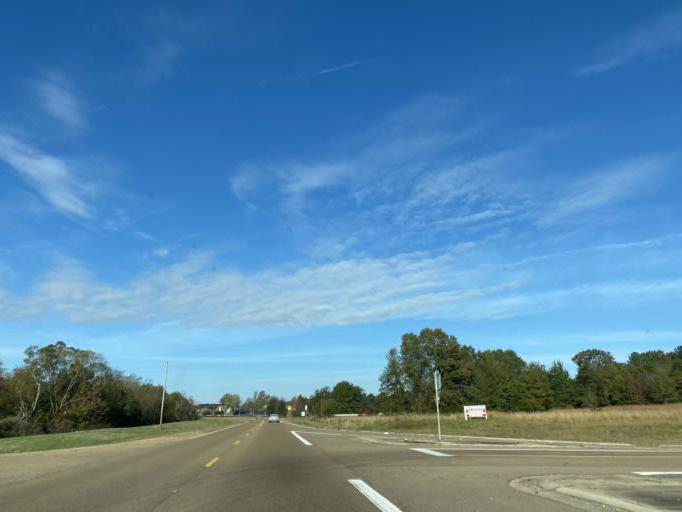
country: US
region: Mississippi
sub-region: Madison County
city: Madison
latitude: 32.4786
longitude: -90.1567
